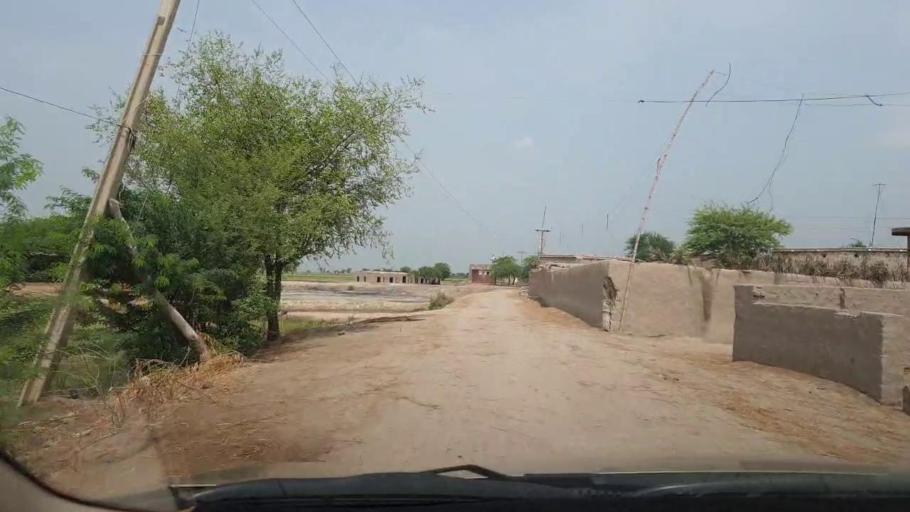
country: PK
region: Sindh
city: Goth Garelo
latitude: 27.5095
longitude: 68.1323
